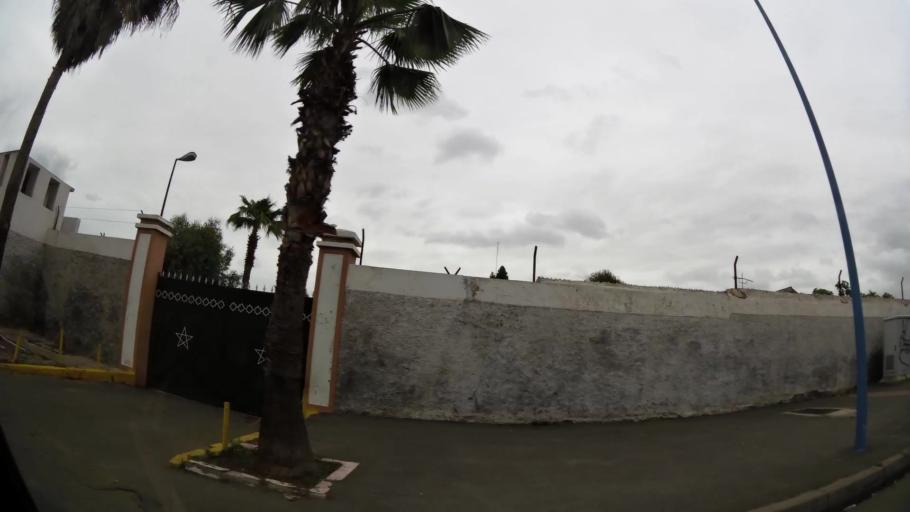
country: MA
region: Grand Casablanca
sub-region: Casablanca
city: Casablanca
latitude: 33.5672
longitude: -7.5652
